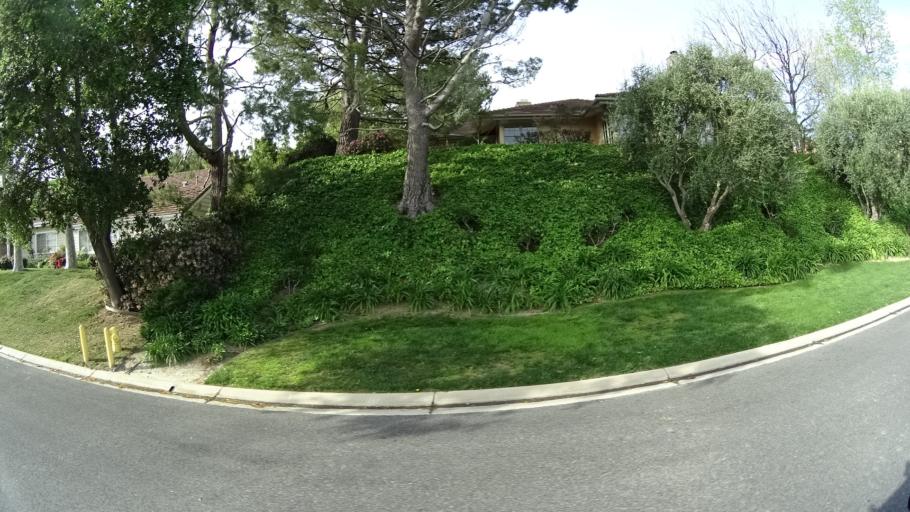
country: US
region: California
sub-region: Ventura County
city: Thousand Oaks
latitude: 34.1898
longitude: -118.8047
